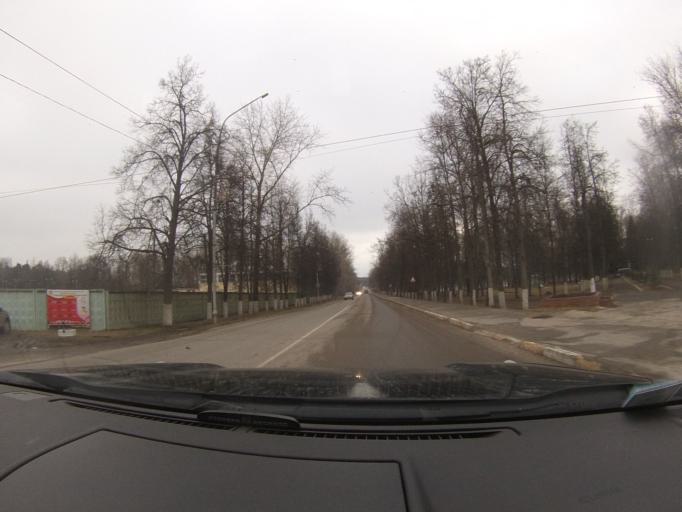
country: RU
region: Moskovskaya
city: Peski
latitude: 55.2531
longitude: 38.7593
